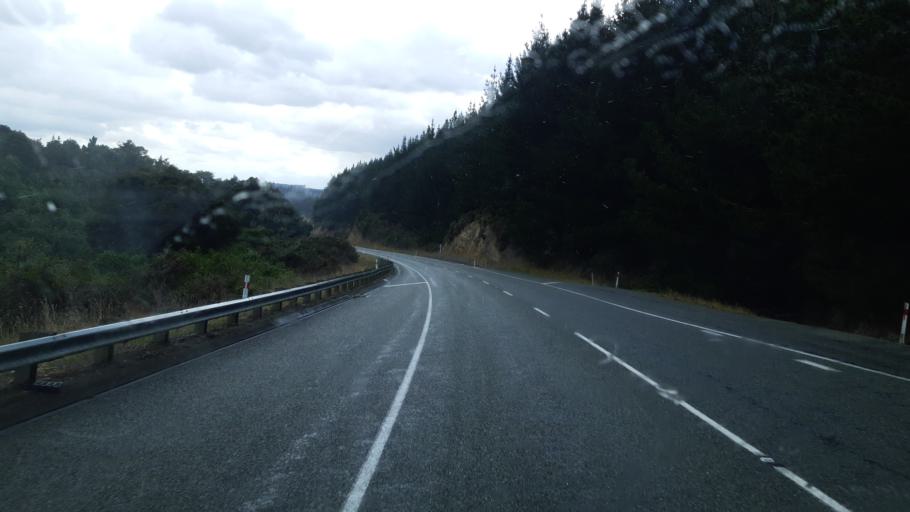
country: NZ
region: Tasman
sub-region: Tasman District
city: Wakefield
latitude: -41.4789
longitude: 172.9274
